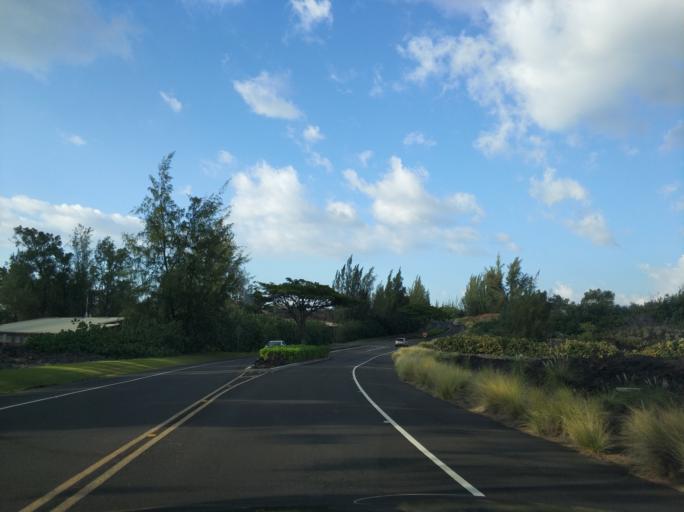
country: US
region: Hawaii
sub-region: Hawaii County
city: Waikoloa Village
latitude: 19.9176
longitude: -155.8767
